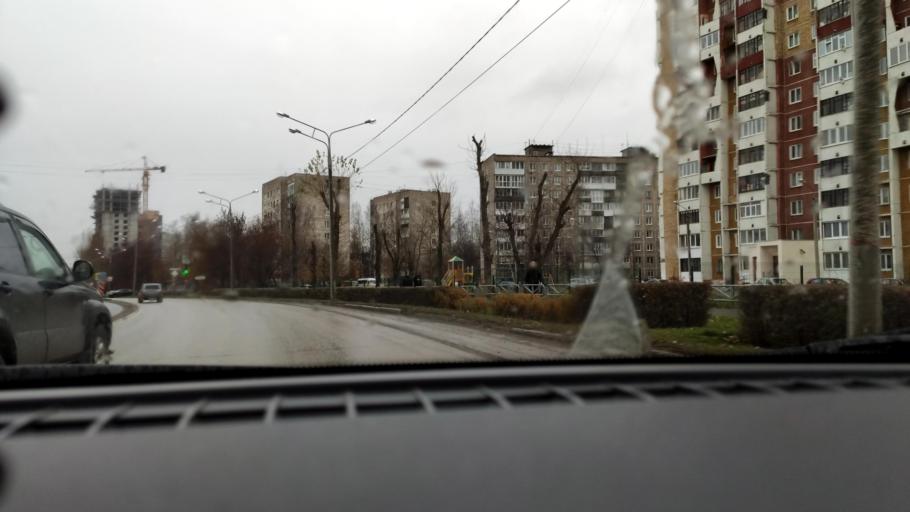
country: RU
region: Perm
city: Perm
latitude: 57.9771
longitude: 56.2150
